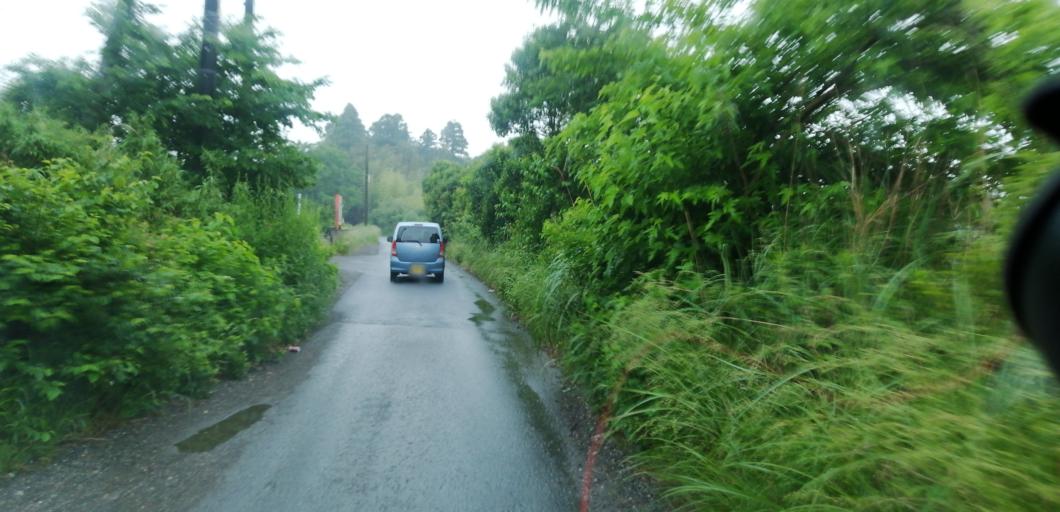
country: JP
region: Chiba
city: Ichihara
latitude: 35.4838
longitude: 140.1472
